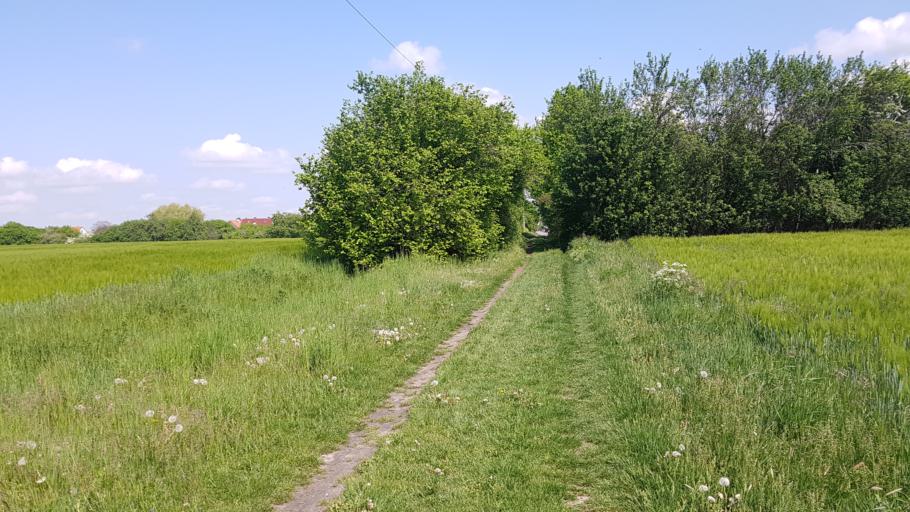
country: DE
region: Brandenburg
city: Doberlug-Kirchhain
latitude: 51.6317
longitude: 13.5528
